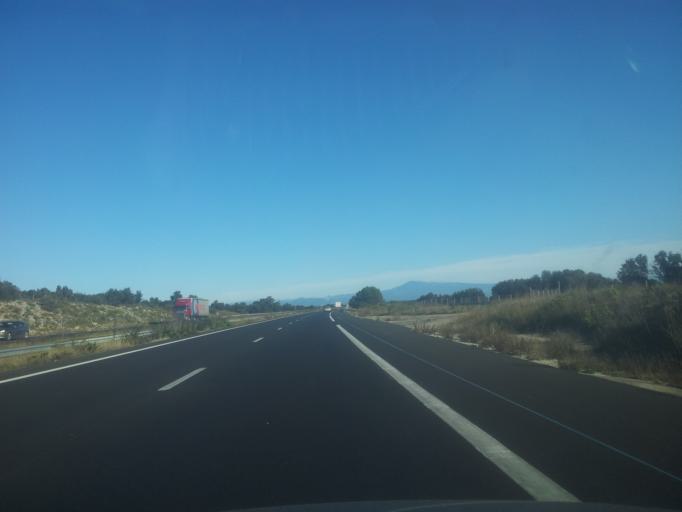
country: FR
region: Languedoc-Roussillon
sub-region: Departement du Gard
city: Rochefort-du-Gard
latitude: 43.9805
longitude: 4.6654
